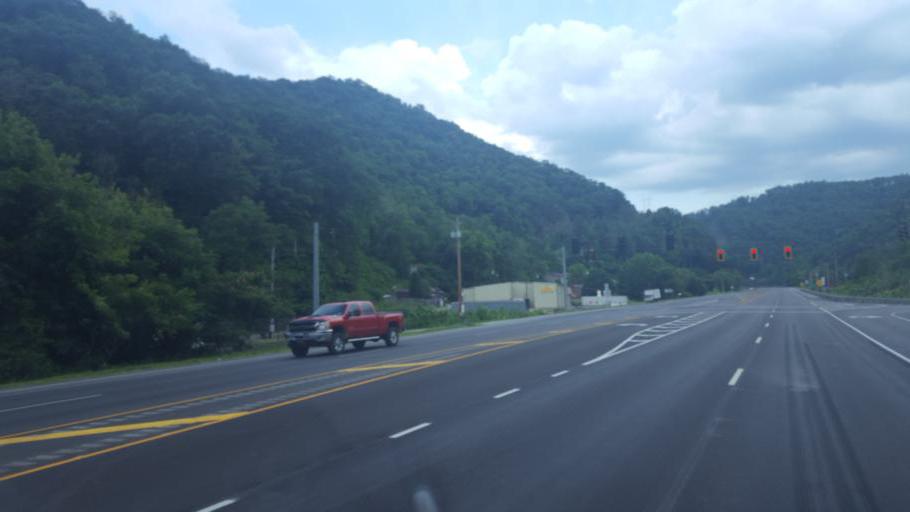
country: US
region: Kentucky
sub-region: Pike County
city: Pikeville
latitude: 37.3609
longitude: -82.5551
